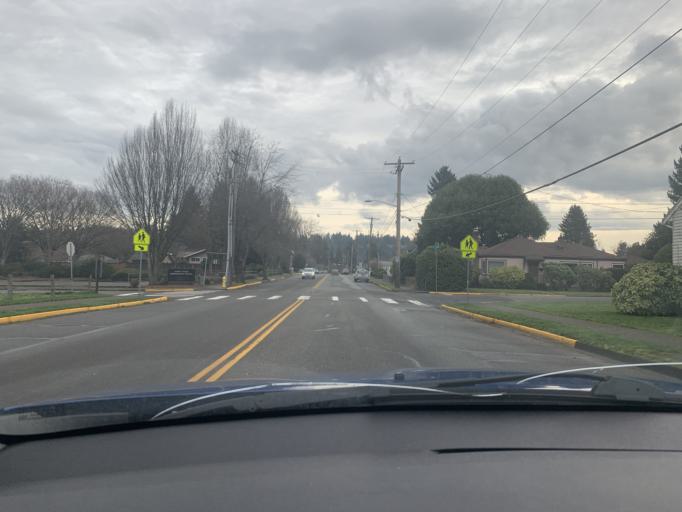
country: US
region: Washington
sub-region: King County
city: Auburn
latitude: 47.3111
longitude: -122.2181
